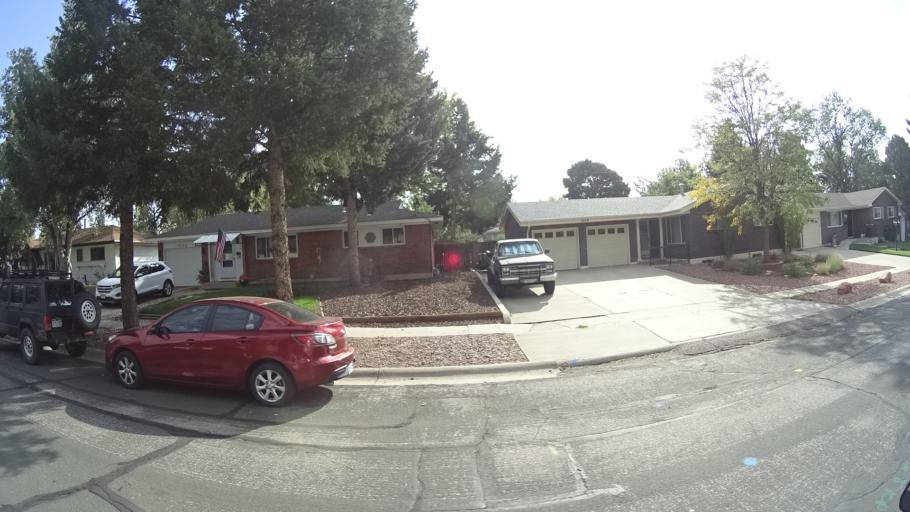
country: US
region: Colorado
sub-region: El Paso County
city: Colorado Springs
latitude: 38.8556
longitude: -104.7633
